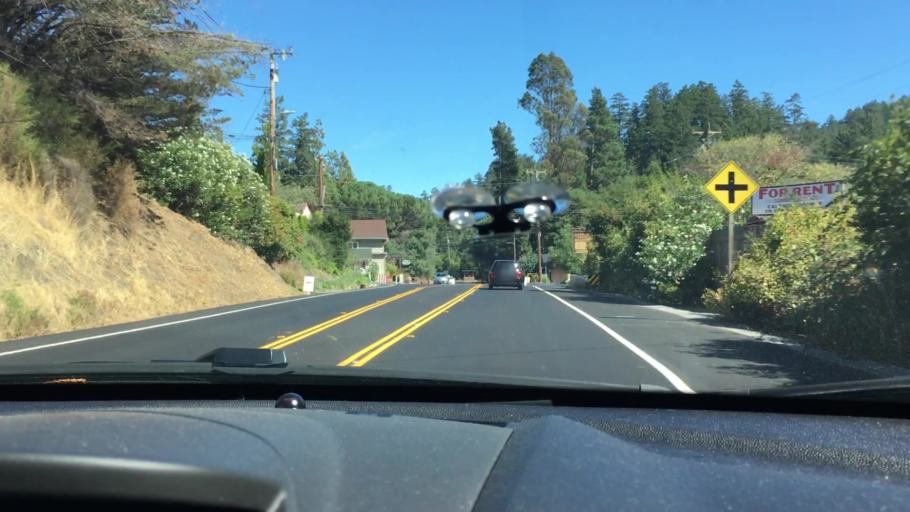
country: US
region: California
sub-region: Marin County
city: Lagunitas-Forest Knolls
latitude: 38.0153
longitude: -122.6896
